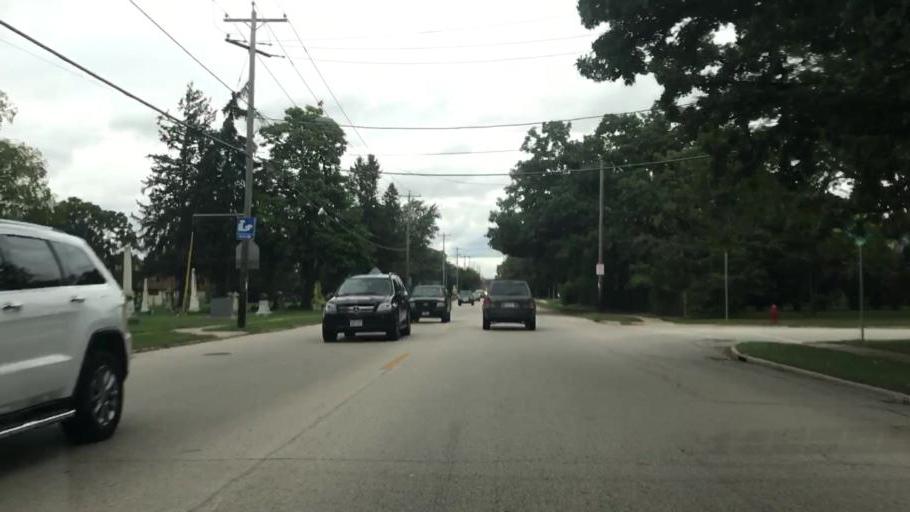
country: US
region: Wisconsin
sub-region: Waukesha County
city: Mukwonago
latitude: 42.8669
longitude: -88.3344
